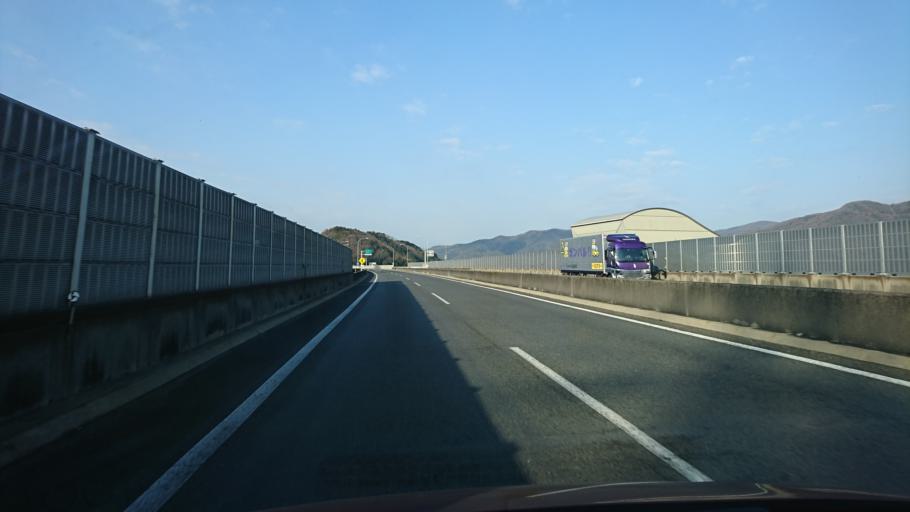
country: JP
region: Hyogo
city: Tatsunocho-tominaga
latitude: 34.8522
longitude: 134.5443
